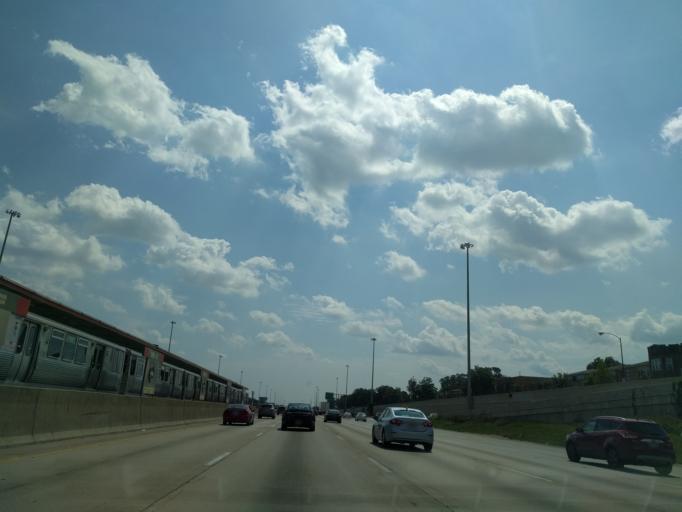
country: US
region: Illinois
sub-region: Cook County
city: Evergreen Park
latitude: 41.7502
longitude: -87.6253
